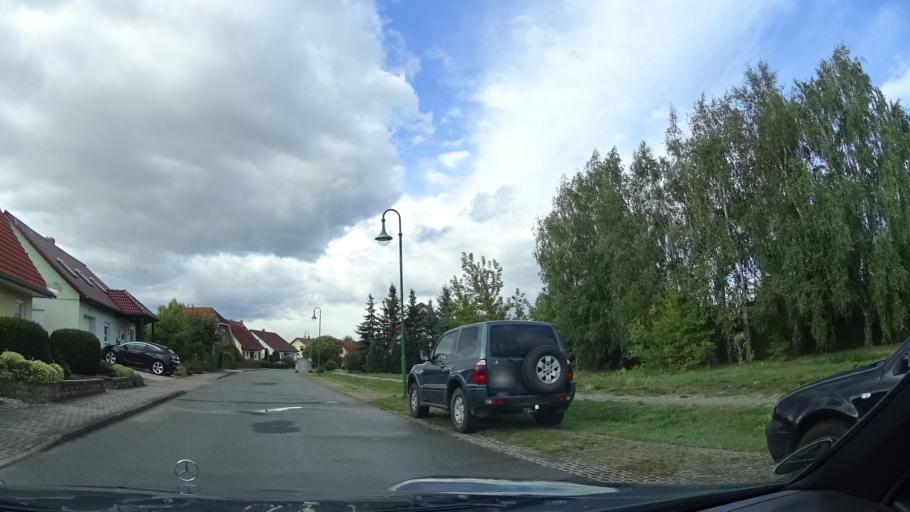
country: DE
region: Brandenburg
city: Neuruppin
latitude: 52.8896
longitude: 12.7917
